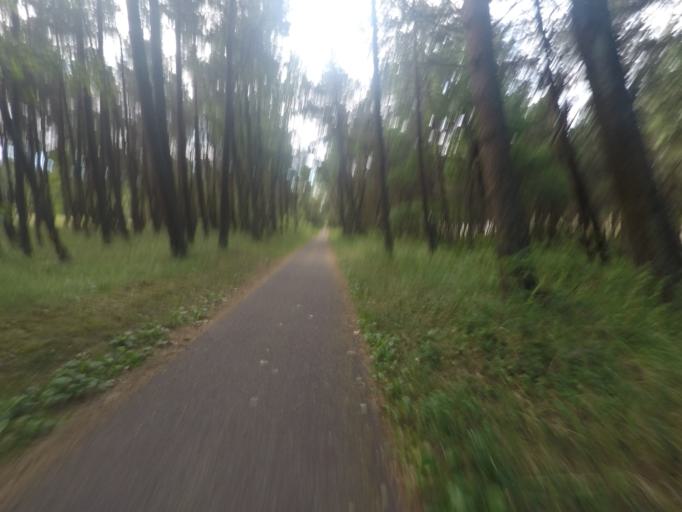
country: LT
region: Klaipedos apskritis
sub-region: Klaipeda
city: Klaipeda
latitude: 55.6517
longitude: 21.1084
